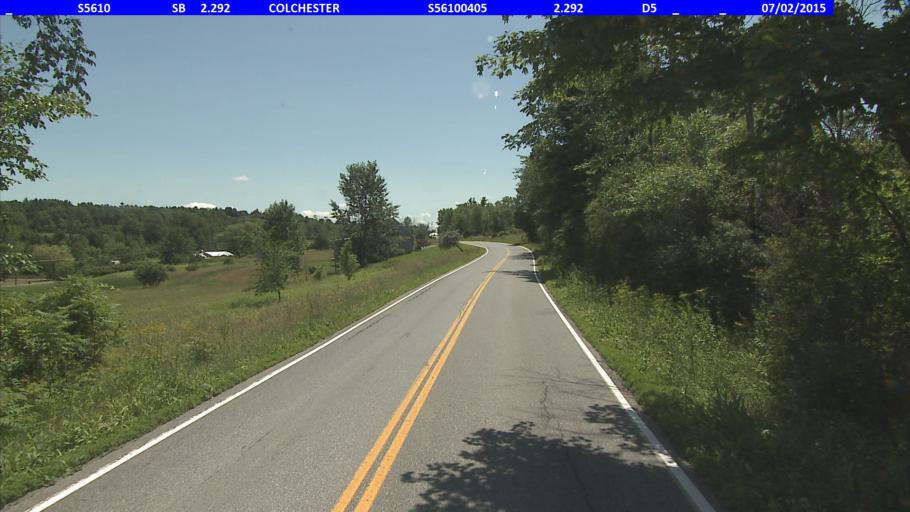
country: US
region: Vermont
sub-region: Chittenden County
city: Colchester
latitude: 44.5726
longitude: -73.1274
